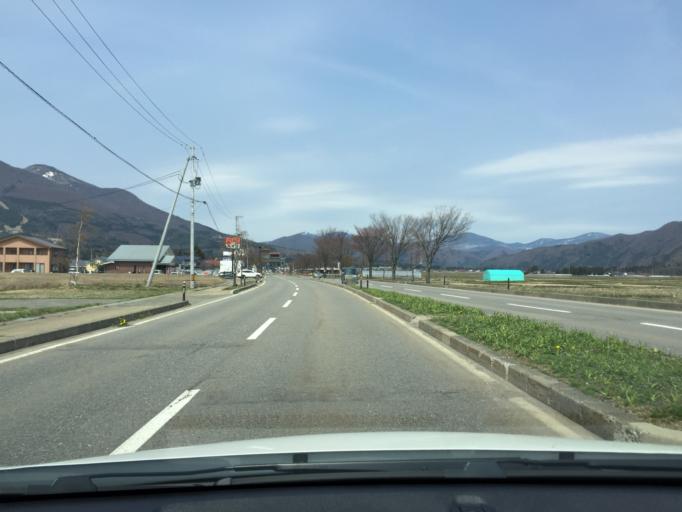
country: JP
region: Fukushima
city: Inawashiro
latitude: 37.5501
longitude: 140.1132
